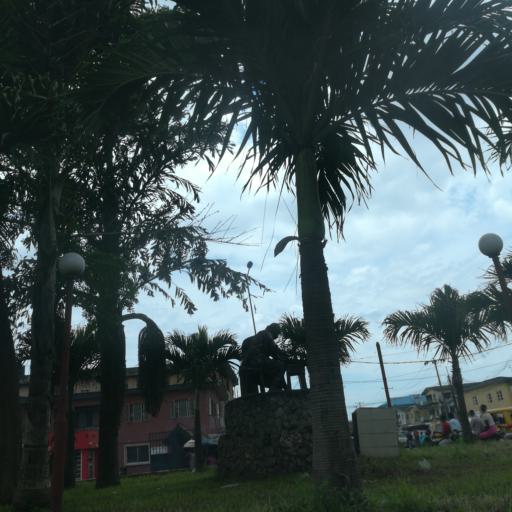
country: NG
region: Lagos
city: Mushin
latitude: 6.5313
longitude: 3.3411
